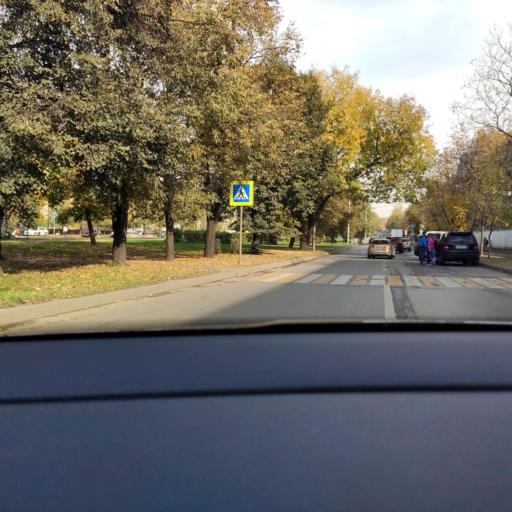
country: RU
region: Moscow
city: Metrogorodok
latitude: 55.8209
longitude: 37.7608
